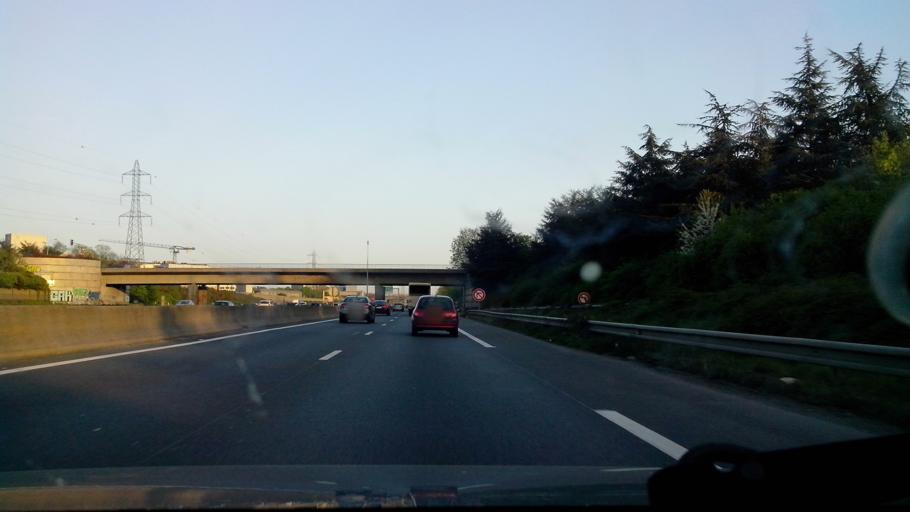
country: FR
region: Ile-de-France
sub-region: Departement de l'Essonne
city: Courcouronnes
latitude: 48.6249
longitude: 2.4176
